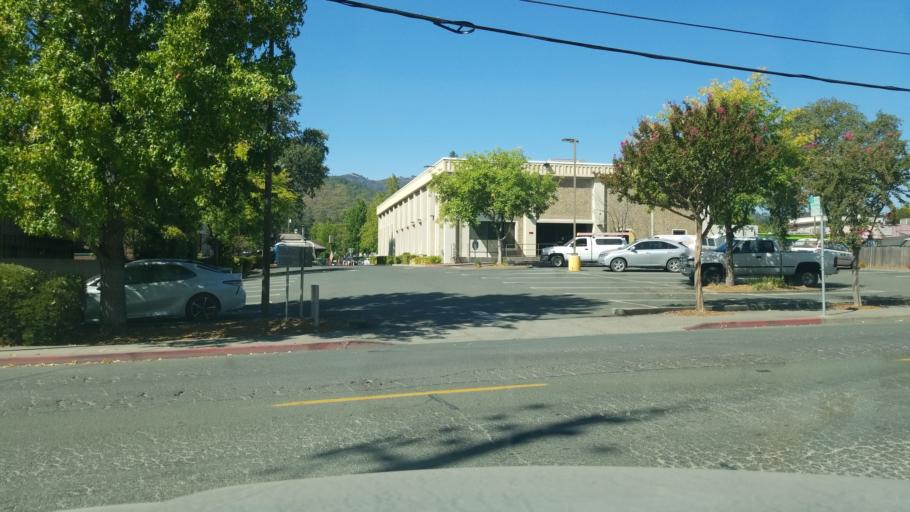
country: US
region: California
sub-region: Mendocino County
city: Ukiah
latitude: 39.1473
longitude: -123.2058
